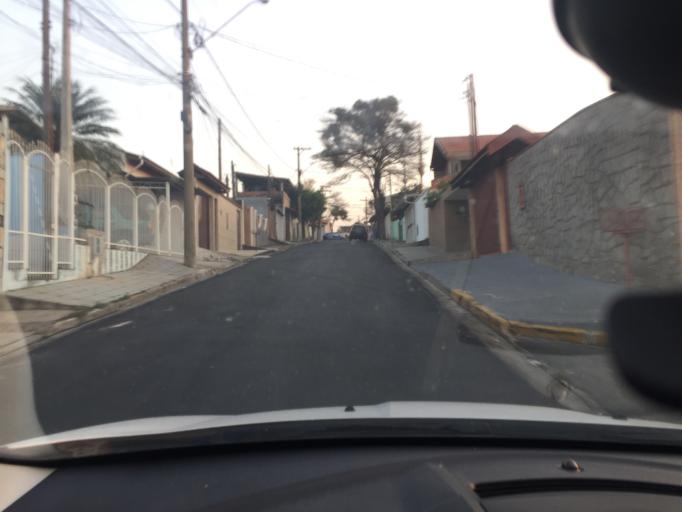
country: BR
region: Sao Paulo
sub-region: Varzea Paulista
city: Varzea Paulista
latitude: -23.2067
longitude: -46.8471
